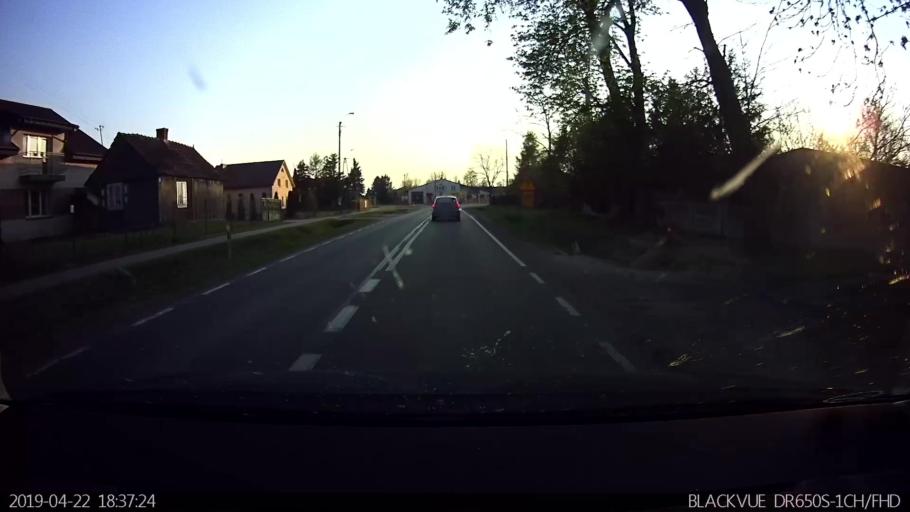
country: PL
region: Masovian Voivodeship
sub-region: Powiat wolominski
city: Klembow
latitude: 52.4426
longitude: 21.3112
